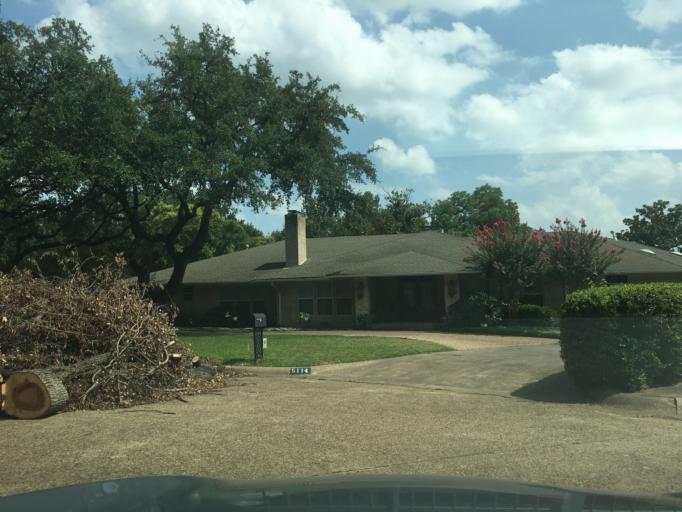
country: US
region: Texas
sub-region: Dallas County
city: University Park
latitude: 32.8985
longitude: -96.8205
